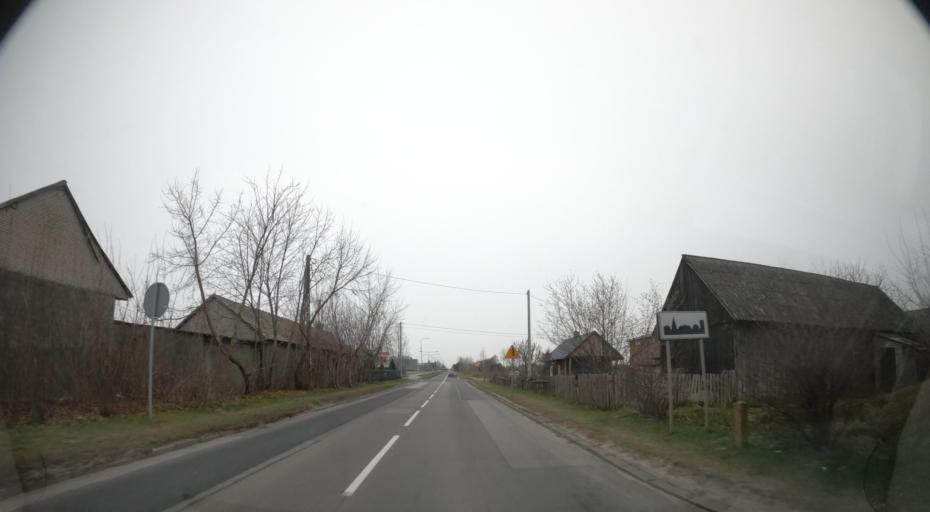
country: PL
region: Masovian Voivodeship
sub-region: Powiat radomski
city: Jastrzebia
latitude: 51.4501
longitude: 21.1937
